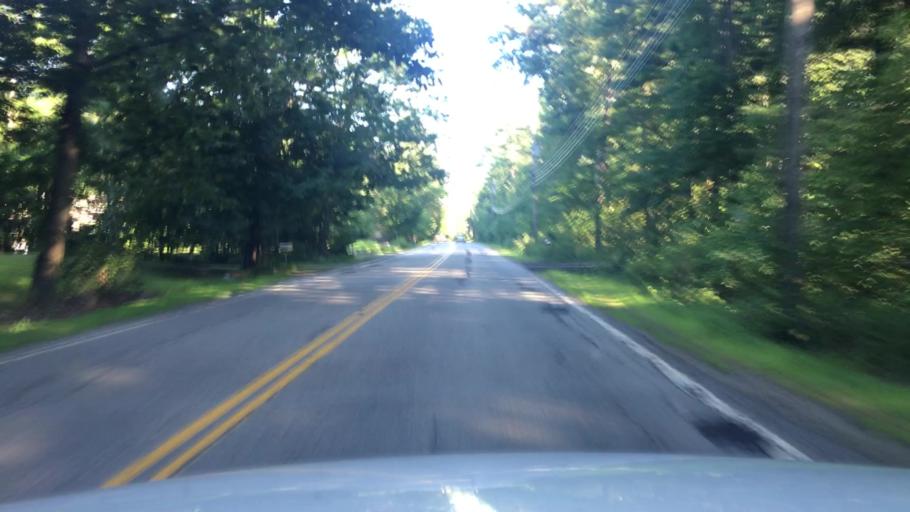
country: US
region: New Hampshire
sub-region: Rockingham County
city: Sandown
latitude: 42.9092
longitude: -71.1592
